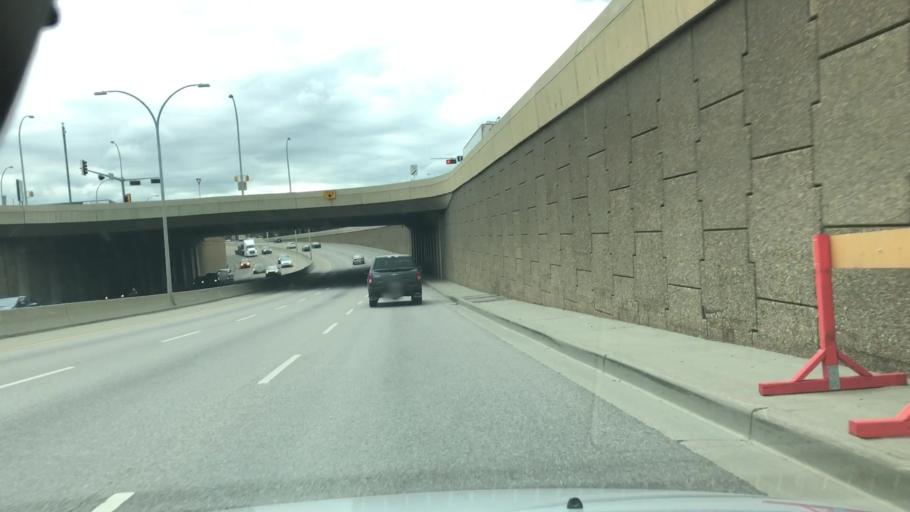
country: CA
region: Alberta
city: Edmonton
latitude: 53.5824
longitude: -113.4660
